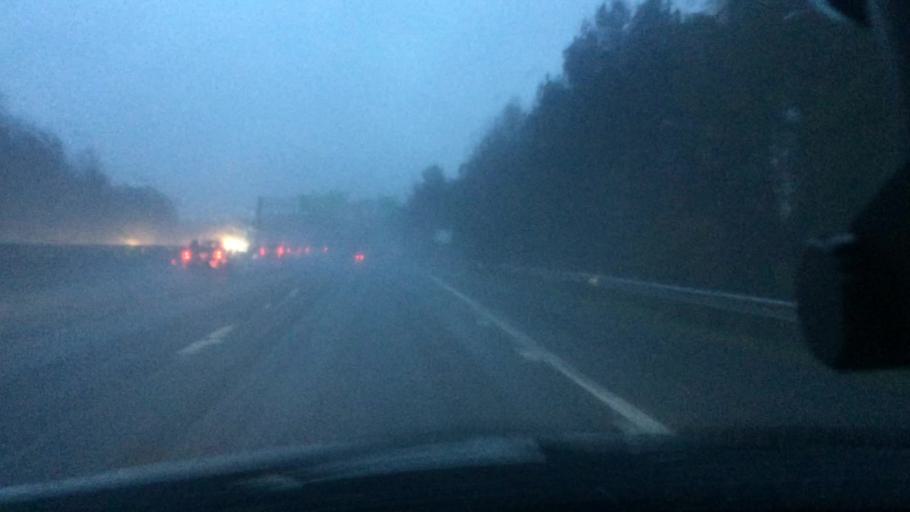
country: US
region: North Carolina
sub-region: Orange County
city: Chapel Hill
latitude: 35.9037
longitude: -78.9656
